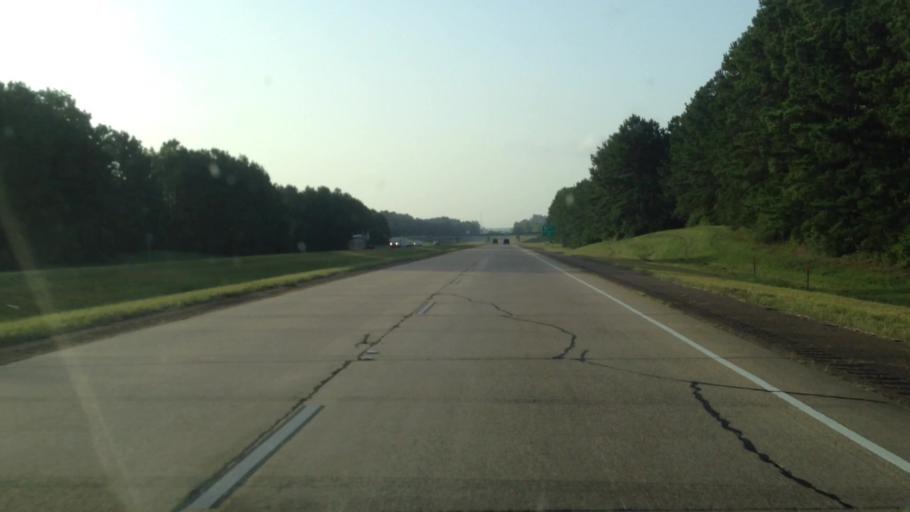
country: US
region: Louisiana
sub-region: Rapides Parish
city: Boyce
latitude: 31.4144
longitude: -92.7241
